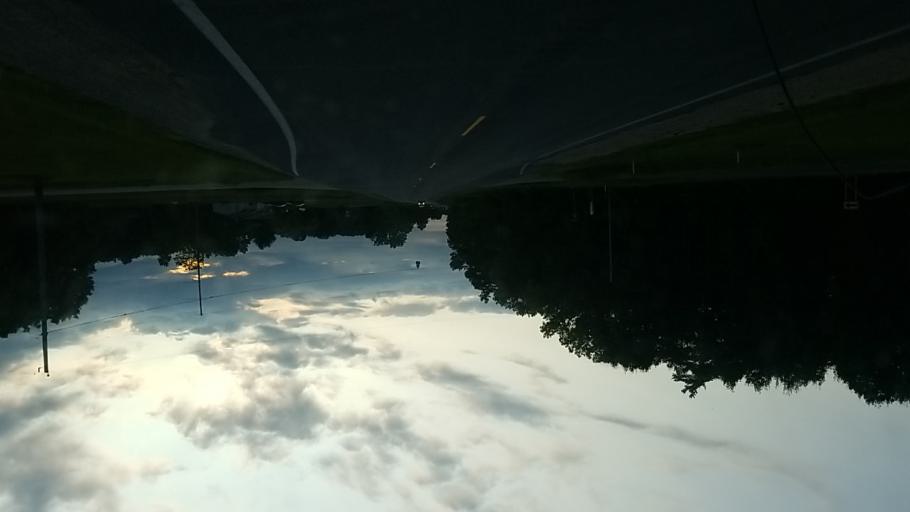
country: US
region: Michigan
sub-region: Newaygo County
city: Newaygo
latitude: 43.4054
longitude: -85.7712
